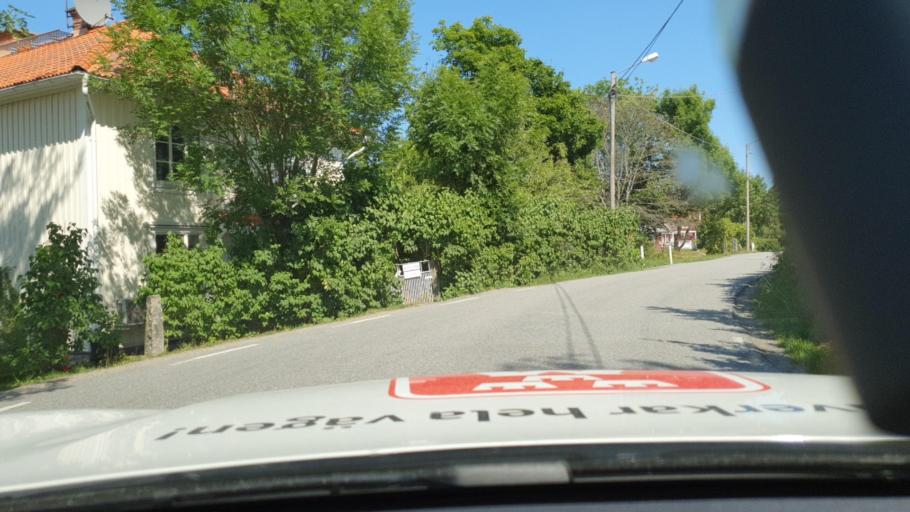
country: SE
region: Stockholm
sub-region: Norrtalje Kommun
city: Bjorko
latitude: 59.8096
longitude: 18.9611
